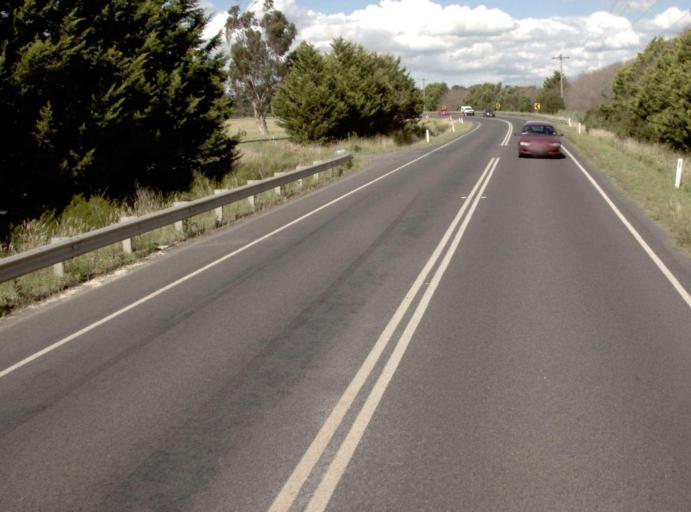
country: AU
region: Victoria
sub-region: Latrobe
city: Morwell
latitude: -38.2943
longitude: 146.4259
